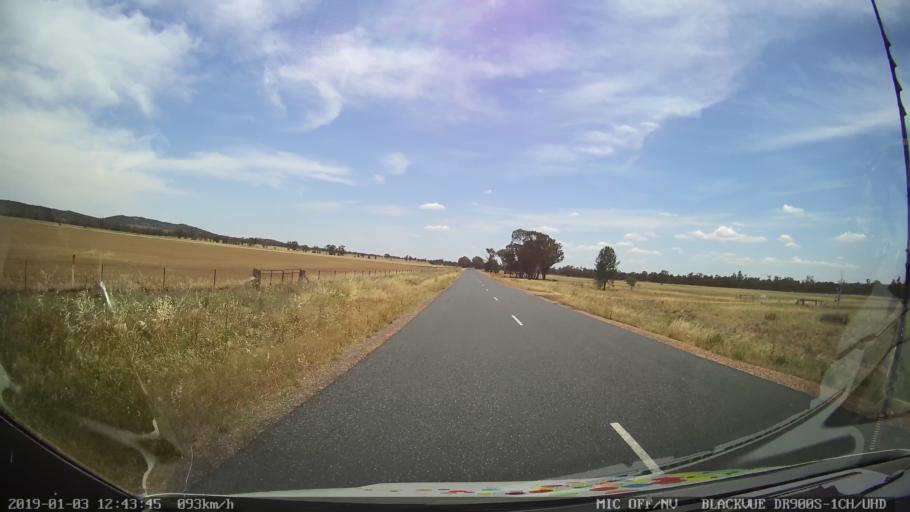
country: AU
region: New South Wales
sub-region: Weddin
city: Grenfell
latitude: -33.7710
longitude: 148.2142
